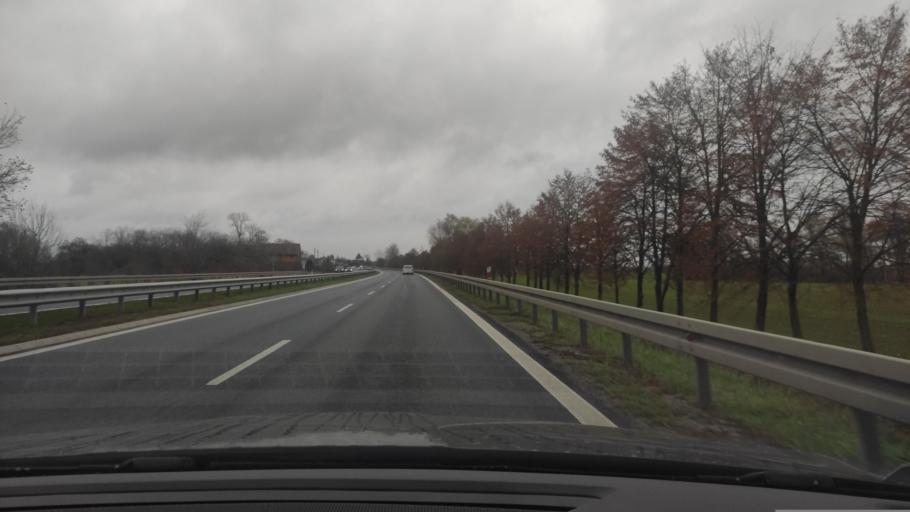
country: PL
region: Greater Poland Voivodeship
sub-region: Powiat poznanski
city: Kostrzyn
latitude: 52.3959
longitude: 17.1817
